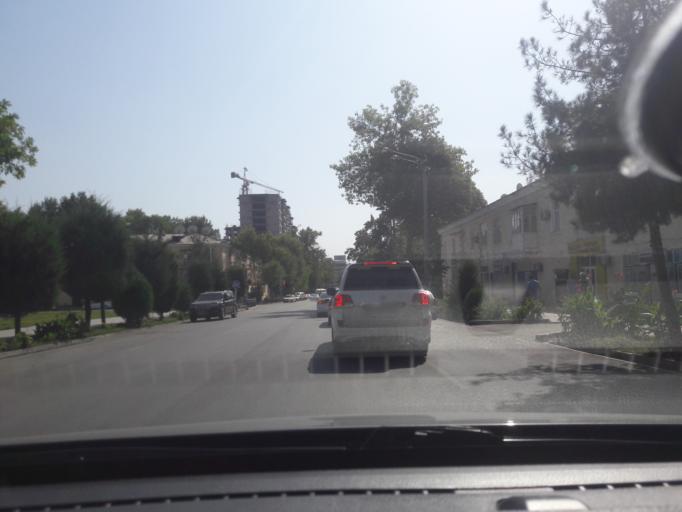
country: TJ
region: Dushanbe
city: Dushanbe
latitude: 38.5663
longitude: 68.7999
